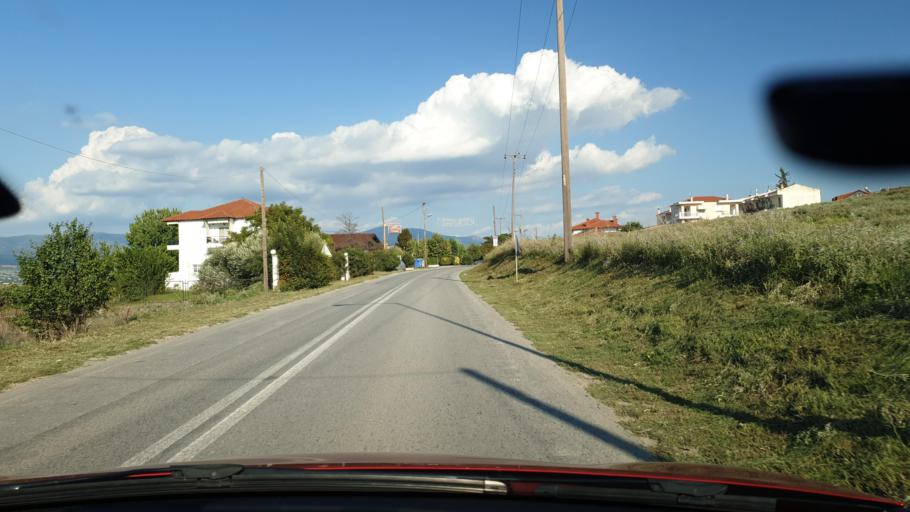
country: GR
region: Central Macedonia
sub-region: Nomos Thessalonikis
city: Agia Paraskevi
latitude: 40.4840
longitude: 23.0454
